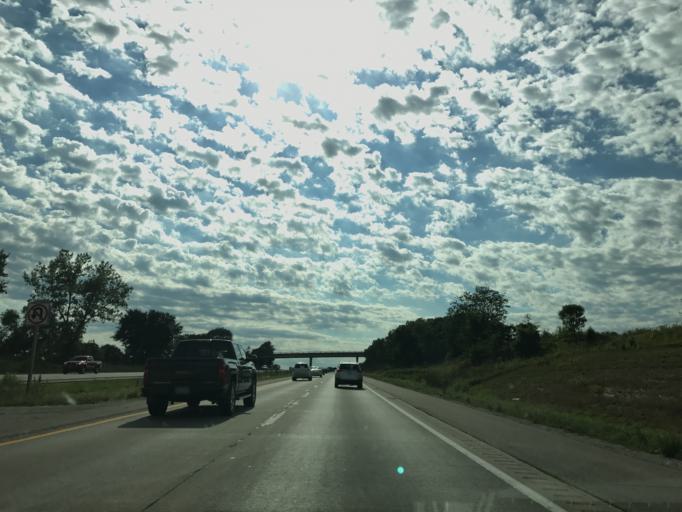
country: US
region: Iowa
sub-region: Dallas County
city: Van Meter
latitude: 41.5450
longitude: -93.9702
